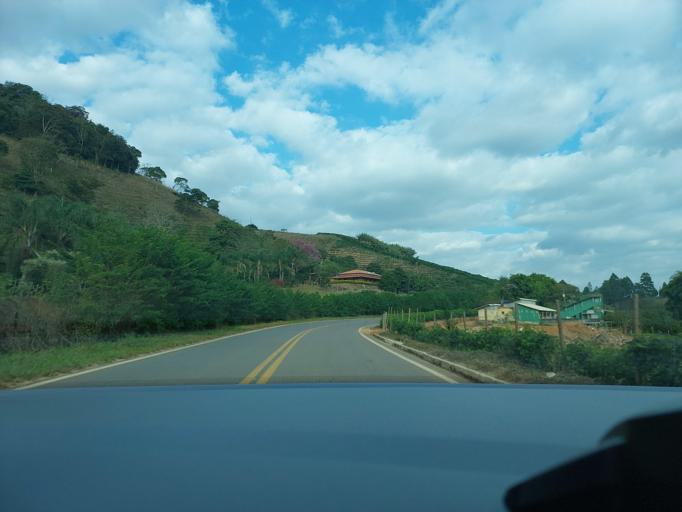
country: BR
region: Minas Gerais
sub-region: Visconde Do Rio Branco
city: Visconde do Rio Branco
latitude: -20.8864
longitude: -42.6594
